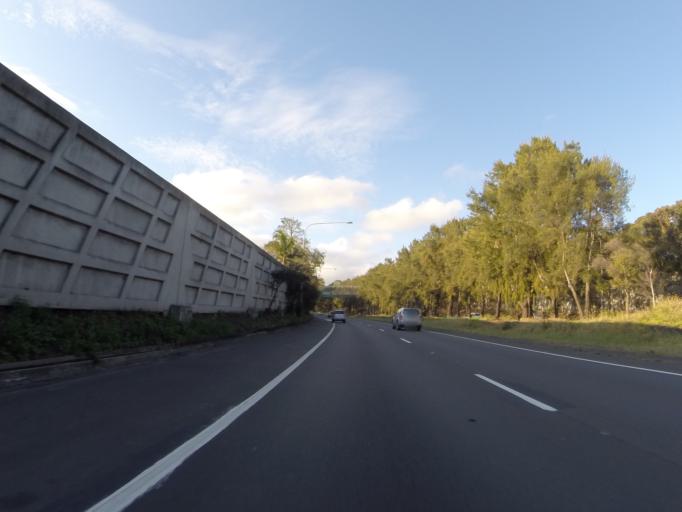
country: AU
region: New South Wales
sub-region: Wollongong
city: Mangerton
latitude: -34.4357
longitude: 150.8680
